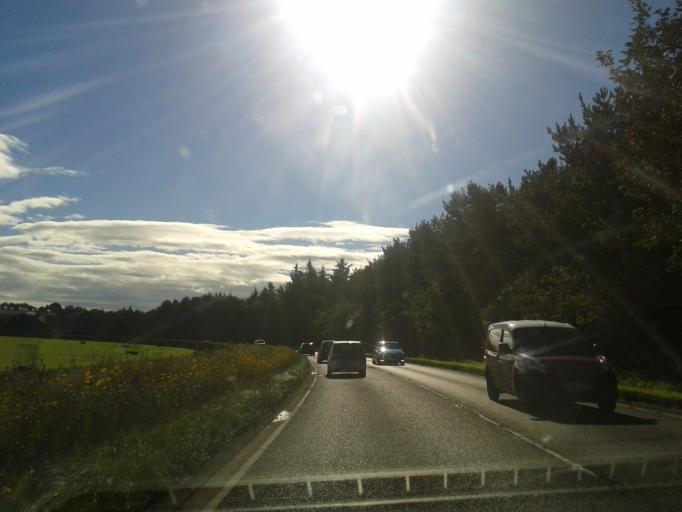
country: GB
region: Scotland
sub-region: Fife
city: Saint Andrews
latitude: 56.3439
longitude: -2.8170
